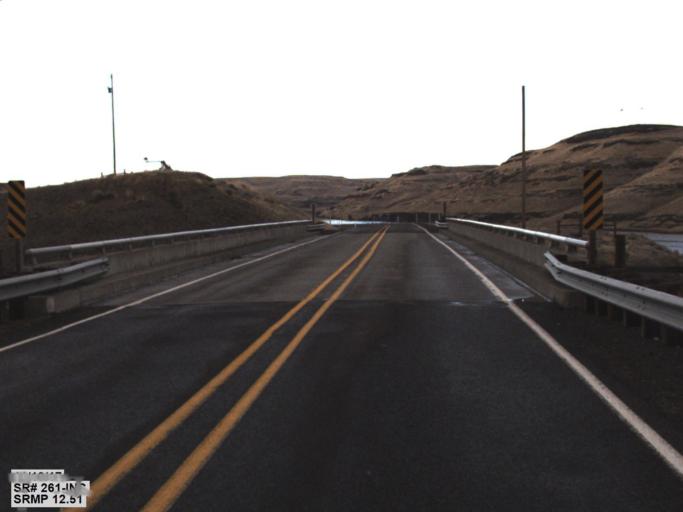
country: US
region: Washington
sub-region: Walla Walla County
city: Waitsburg
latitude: 46.5640
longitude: -118.1862
